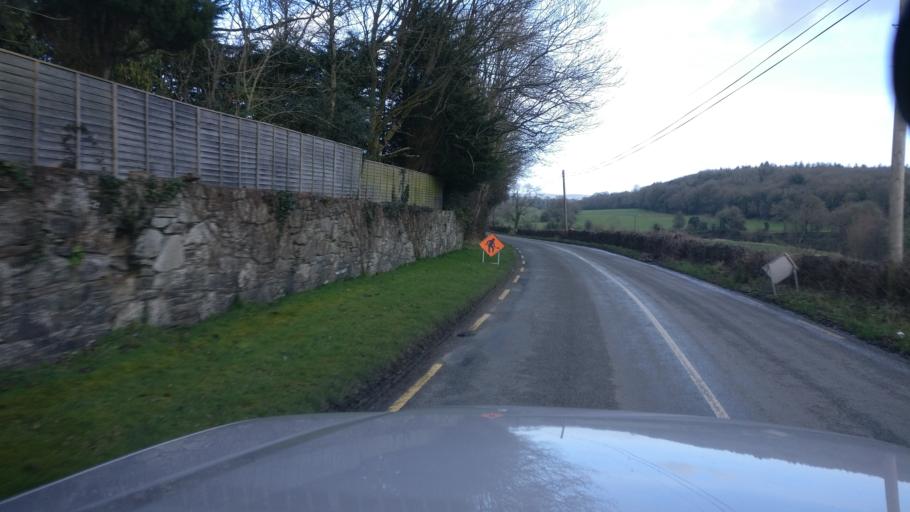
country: IE
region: Leinster
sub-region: Kilkenny
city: Castlecomer
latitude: 52.8165
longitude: -7.2136
